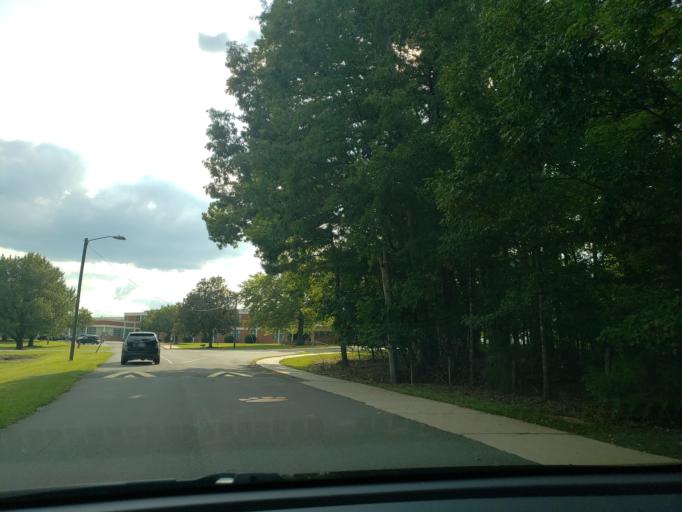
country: US
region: North Carolina
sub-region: Durham County
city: Durham
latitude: 36.0886
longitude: -78.9162
